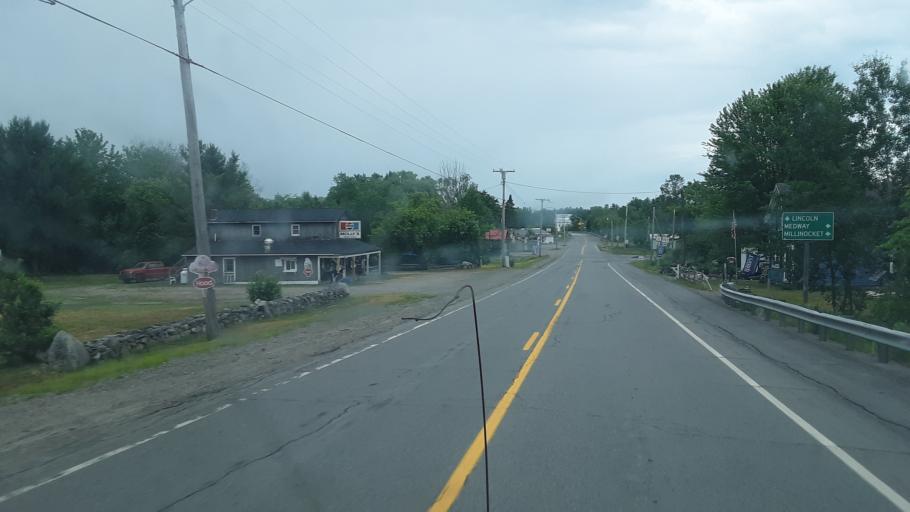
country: US
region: Maine
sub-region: Penobscot County
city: Medway
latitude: 45.5223
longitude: -68.3514
